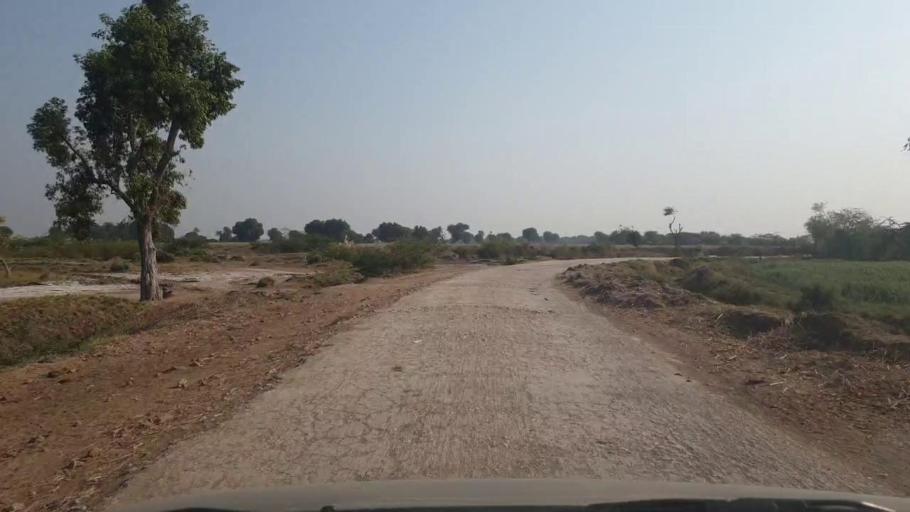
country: PK
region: Sindh
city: Digri
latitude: 25.2527
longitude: 69.1830
